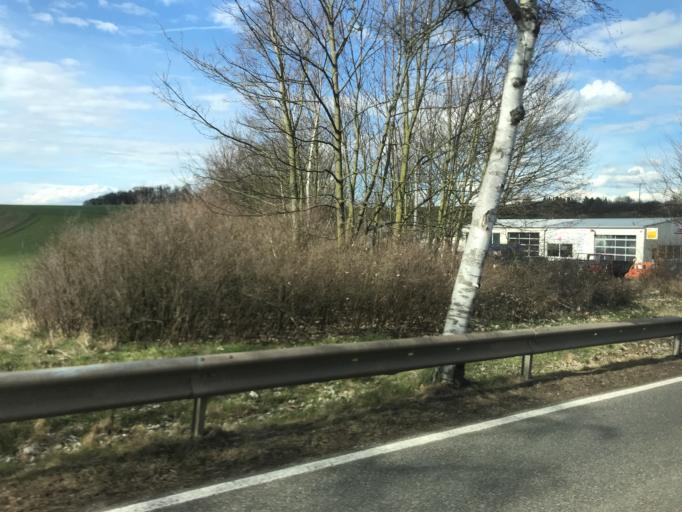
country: DE
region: Rheinland-Pfalz
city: Wassenach
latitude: 50.4386
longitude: 7.2786
